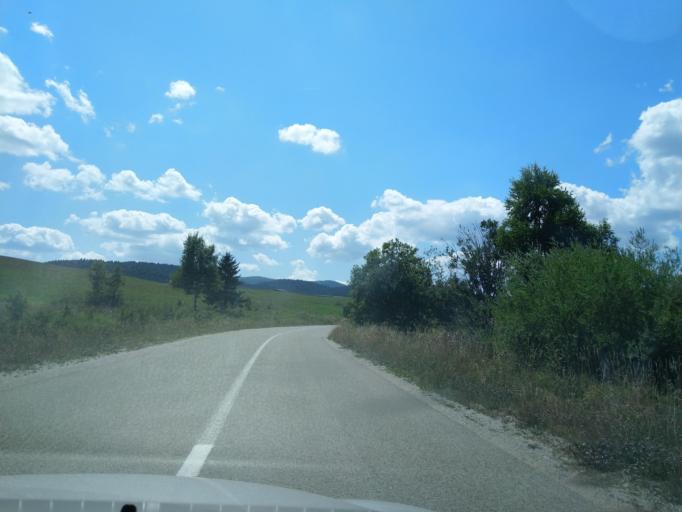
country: RS
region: Central Serbia
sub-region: Zlatiborski Okrug
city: Sjenica
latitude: 43.3294
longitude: 19.8726
